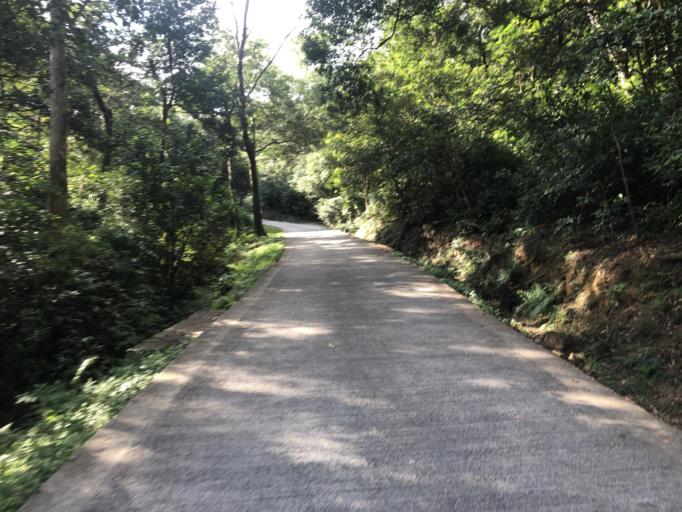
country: HK
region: Tsuen Wan
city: Tsuen Wan
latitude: 22.4074
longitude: 114.1032
